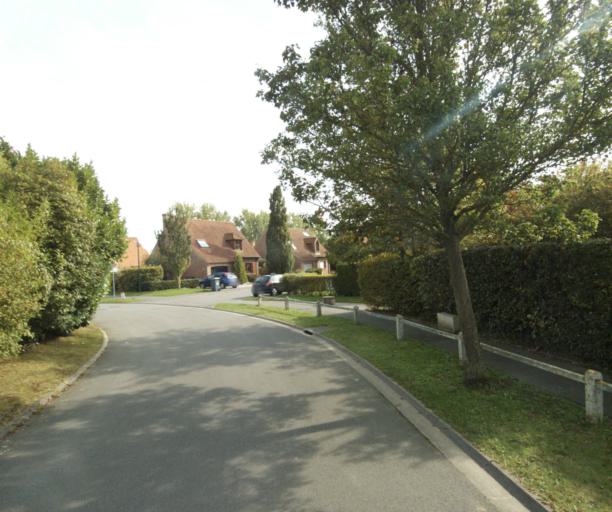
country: FR
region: Nord-Pas-de-Calais
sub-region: Departement du Nord
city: Radinghem-en-Weppes
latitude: 50.6006
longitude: 2.9213
